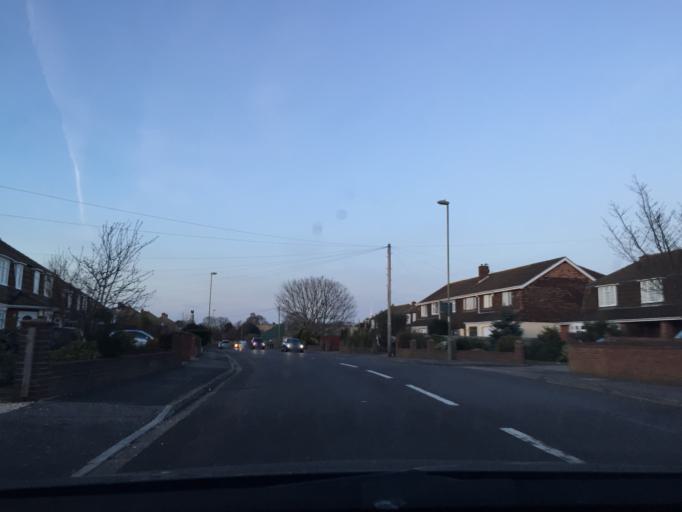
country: GB
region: England
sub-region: Hampshire
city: Gosport
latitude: 50.7803
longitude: -1.1315
